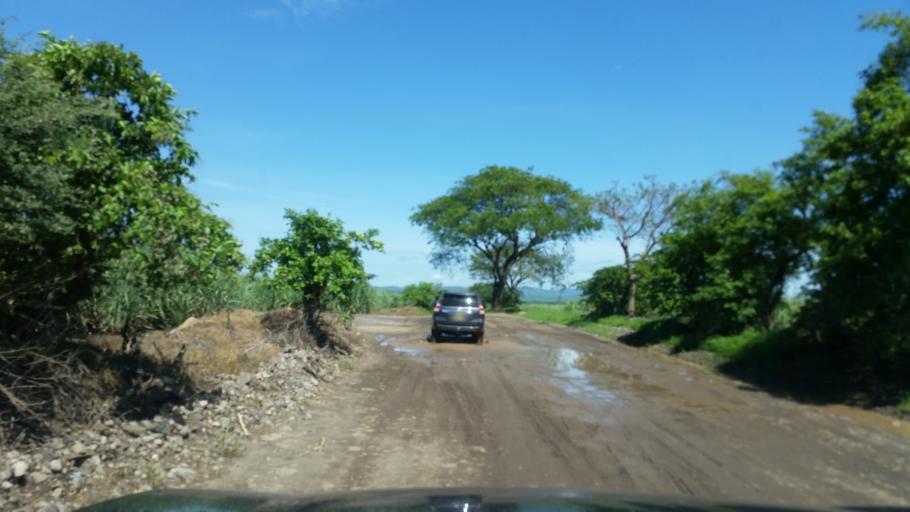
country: NI
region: Chinandega
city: Puerto Morazan
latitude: 12.7741
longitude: -87.1034
